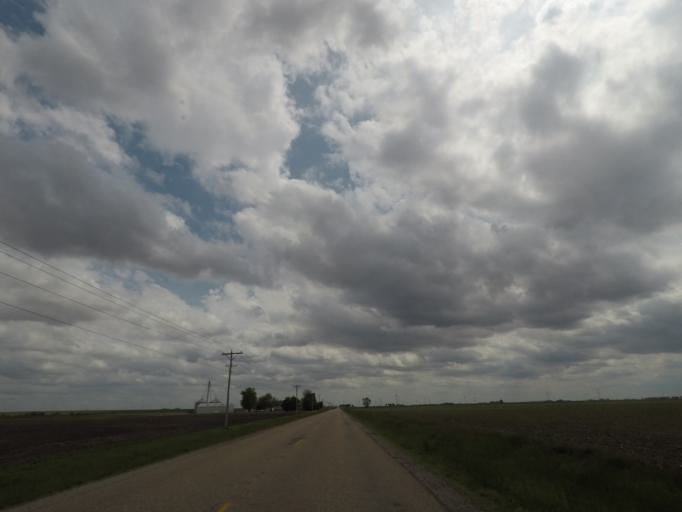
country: US
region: Illinois
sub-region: Macon County
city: Maroa
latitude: 40.0773
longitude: -89.0859
